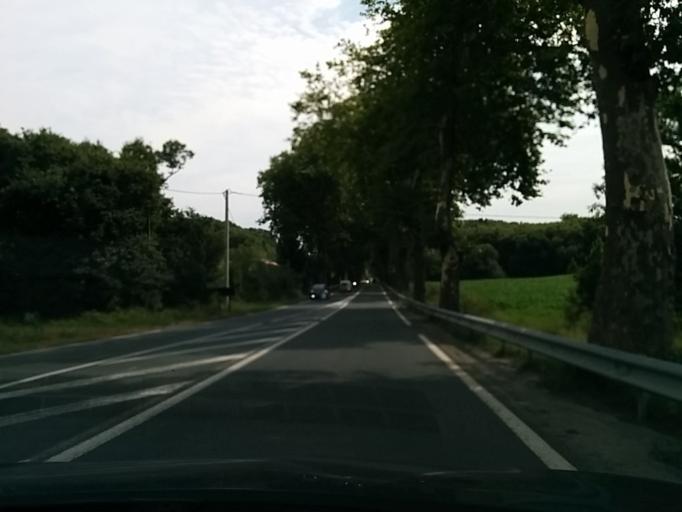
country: FR
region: Aquitaine
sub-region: Departement des Pyrenees-Atlantiques
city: Urrugne
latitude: 43.3603
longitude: -1.7249
